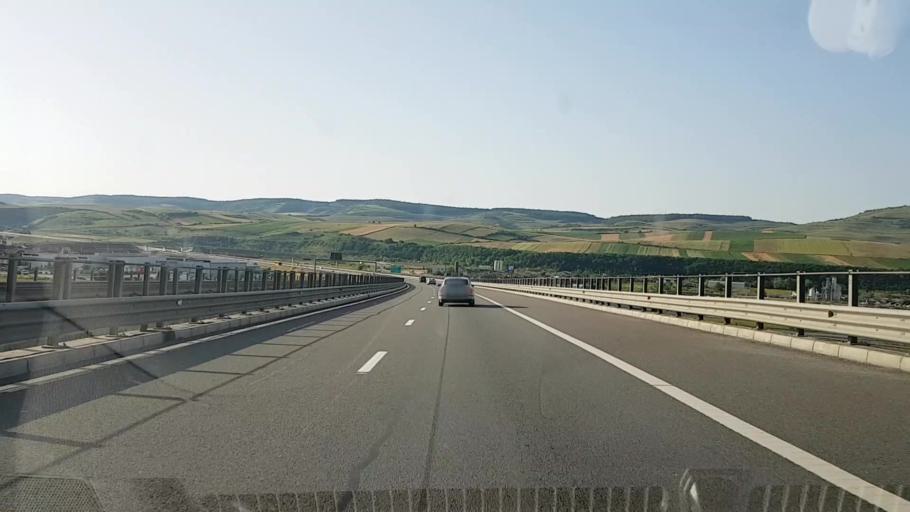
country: RO
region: Cluj
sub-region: Comuna Floresti
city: Luna de Sus
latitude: 46.7479
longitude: 23.4179
